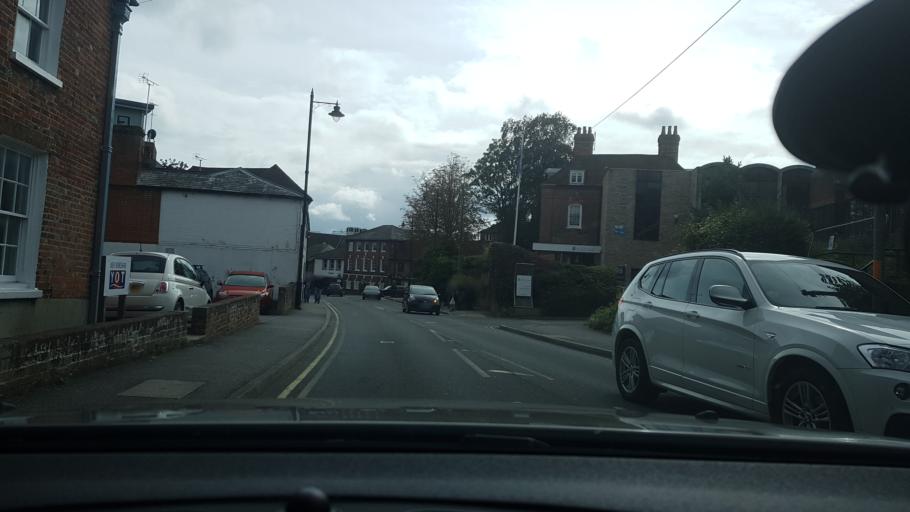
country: GB
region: England
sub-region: West Berkshire
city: Newbury
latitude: 51.4068
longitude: -1.3279
